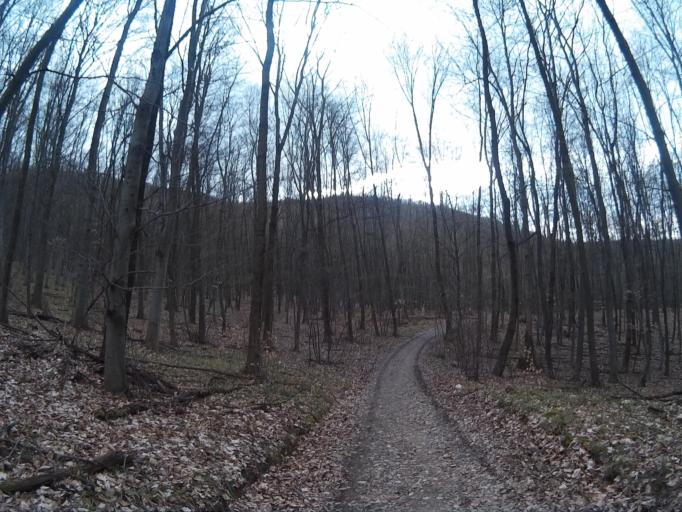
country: HU
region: Pest
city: Kosd
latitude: 47.8420
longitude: 19.1330
